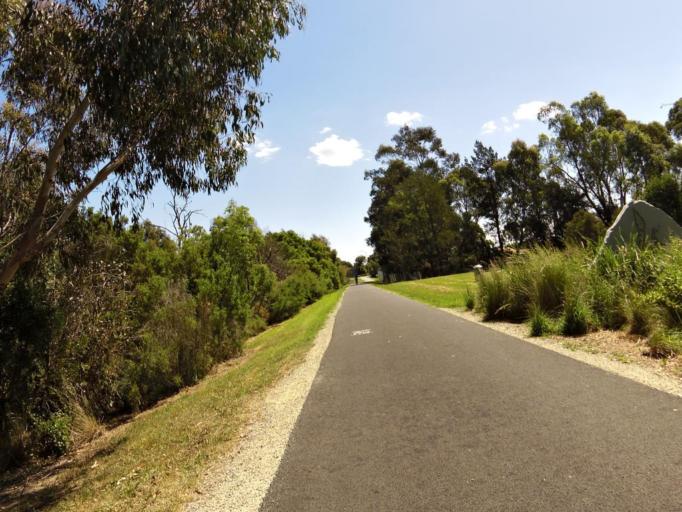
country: AU
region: Victoria
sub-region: Knox
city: Knoxfield
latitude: -37.9000
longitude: 145.2598
